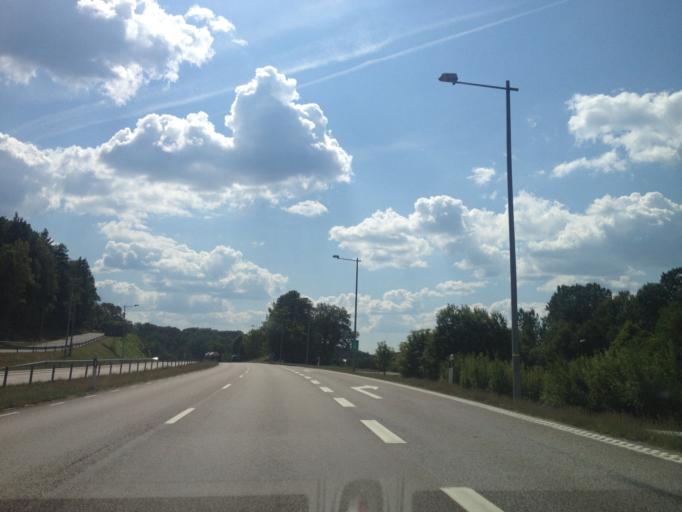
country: SE
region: Vaestra Goetaland
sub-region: Alingsas Kommun
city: Ingared
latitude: 57.8178
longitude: 12.4170
